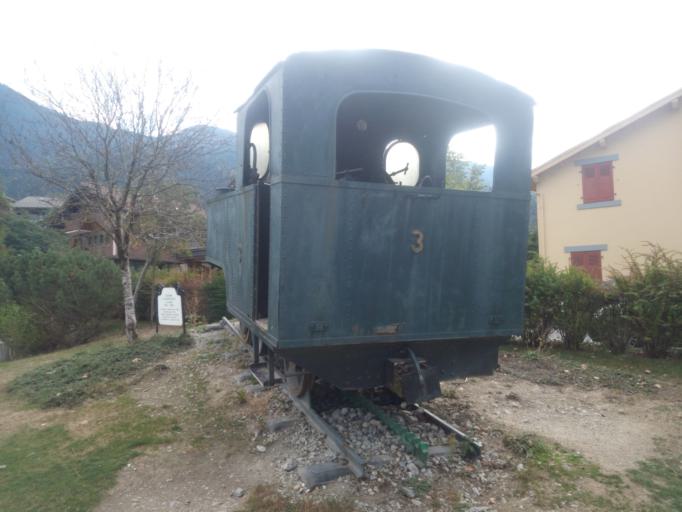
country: FR
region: Rhone-Alpes
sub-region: Departement de la Haute-Savoie
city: Saint-Gervais-les-Bains
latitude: 45.9062
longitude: 6.7018
